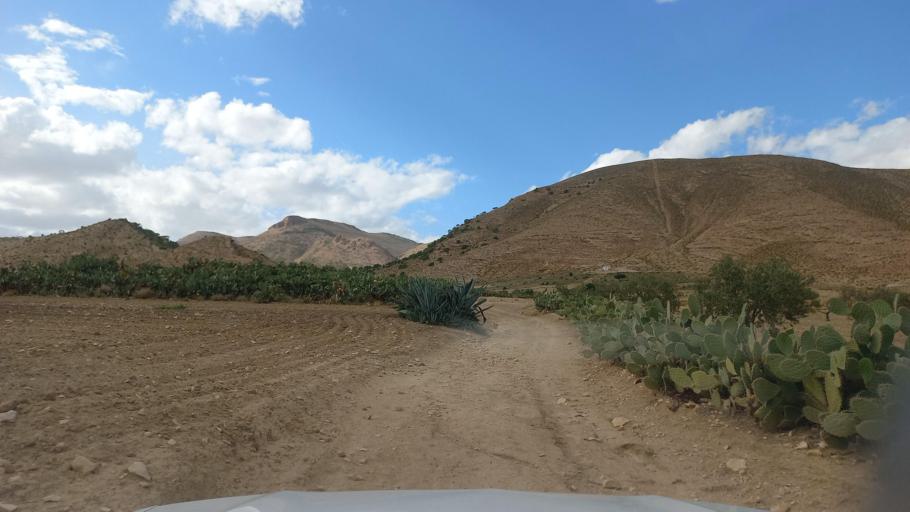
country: TN
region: Al Qasrayn
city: Sbiba
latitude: 35.4523
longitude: 9.0631
